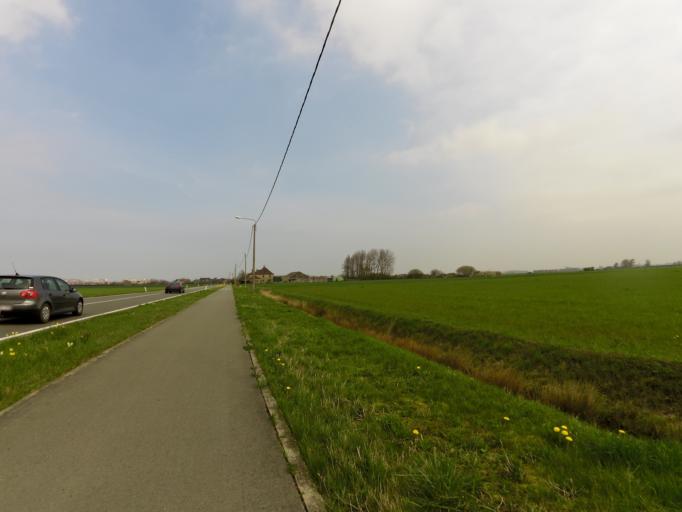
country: BE
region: Flanders
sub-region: Provincie West-Vlaanderen
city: Middelkerke
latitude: 51.1692
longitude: 2.8281
